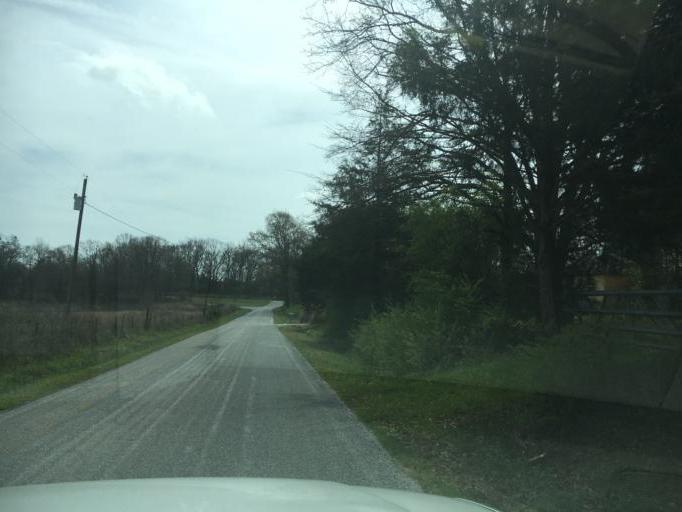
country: US
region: Georgia
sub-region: Hart County
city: Royston
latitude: 34.3589
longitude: -83.0476
